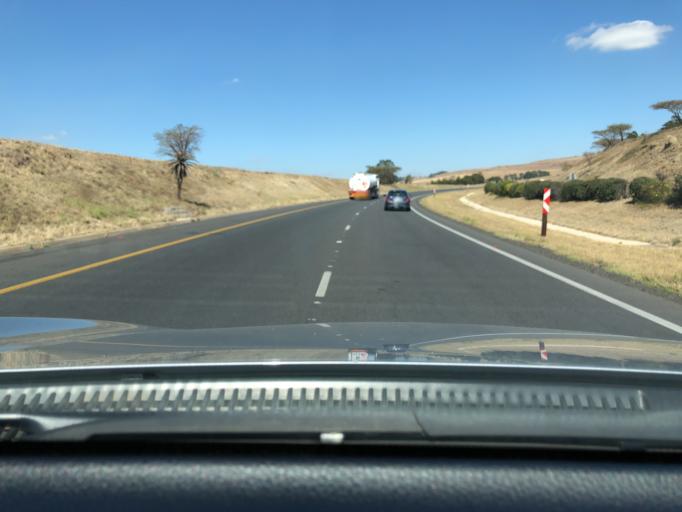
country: ZA
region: KwaZulu-Natal
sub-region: uThukela District Municipality
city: Estcourt
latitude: -29.0710
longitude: 29.9223
